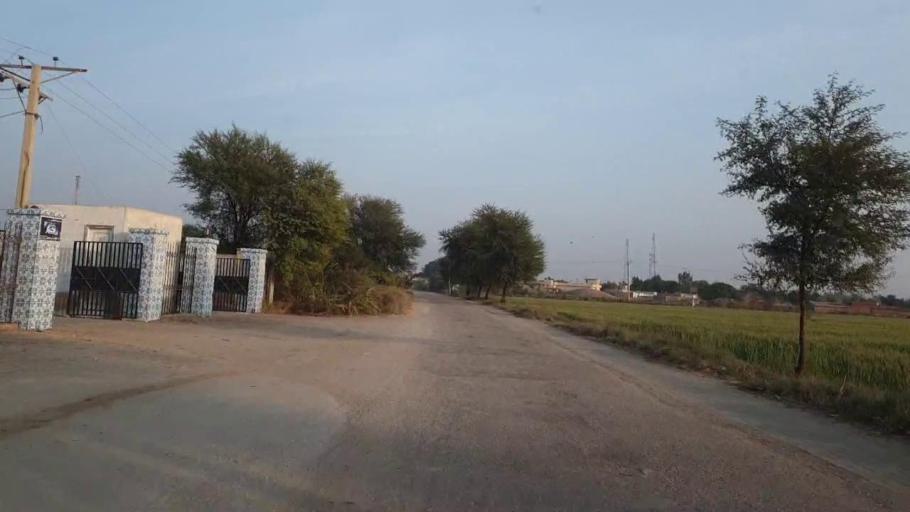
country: PK
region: Sindh
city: Matiari
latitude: 25.6029
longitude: 68.4385
